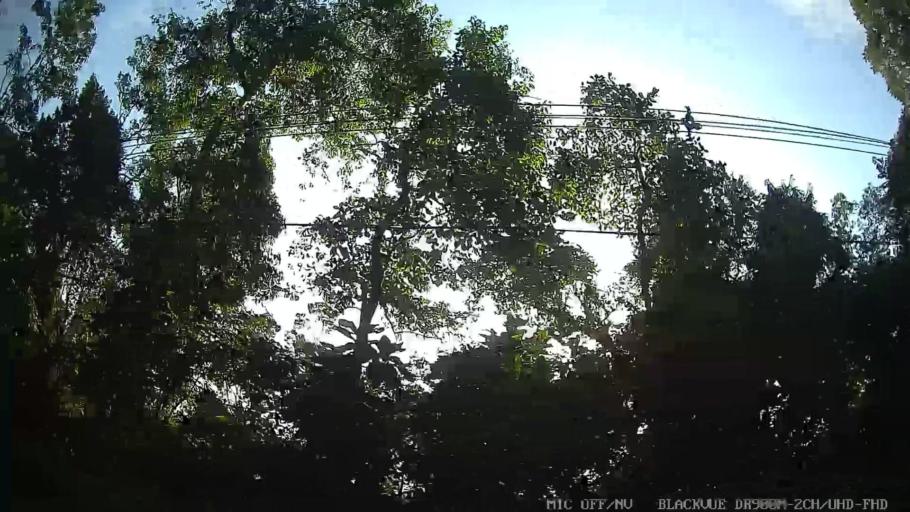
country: BR
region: Sao Paulo
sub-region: Guaruja
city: Guaruja
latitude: -23.9831
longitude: -46.2590
